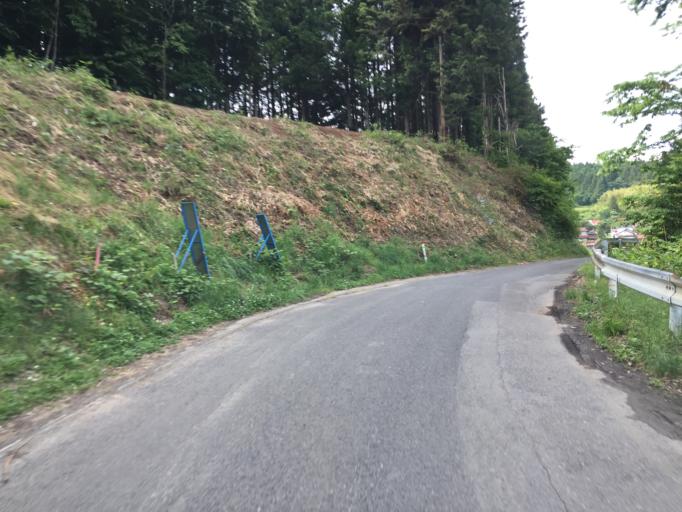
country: JP
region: Fukushima
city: Funehikimachi-funehiki
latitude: 37.5112
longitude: 140.6497
